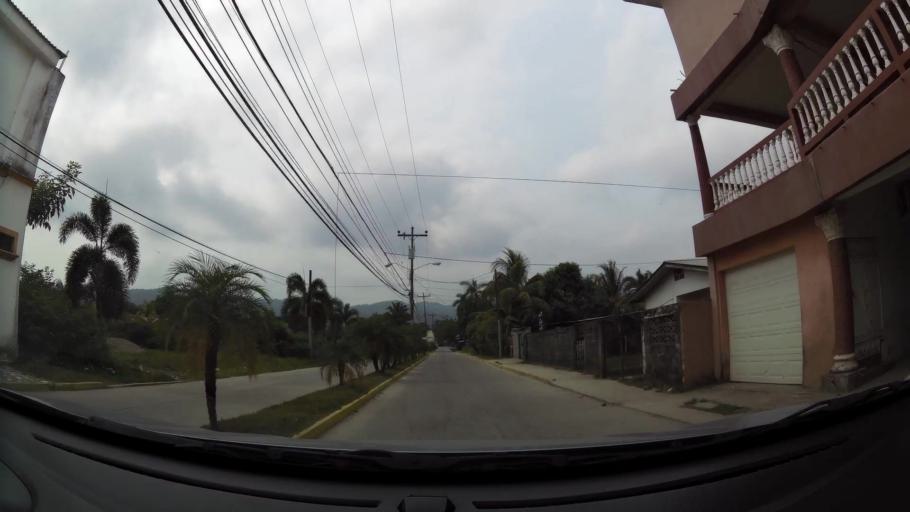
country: HN
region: Atlantida
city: Tela
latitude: 15.7647
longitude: -87.4802
